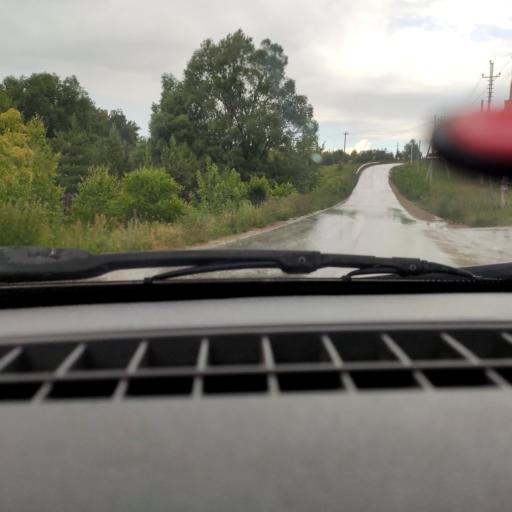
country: RU
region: Bashkortostan
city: Kabakovo
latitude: 54.5653
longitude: 56.2710
